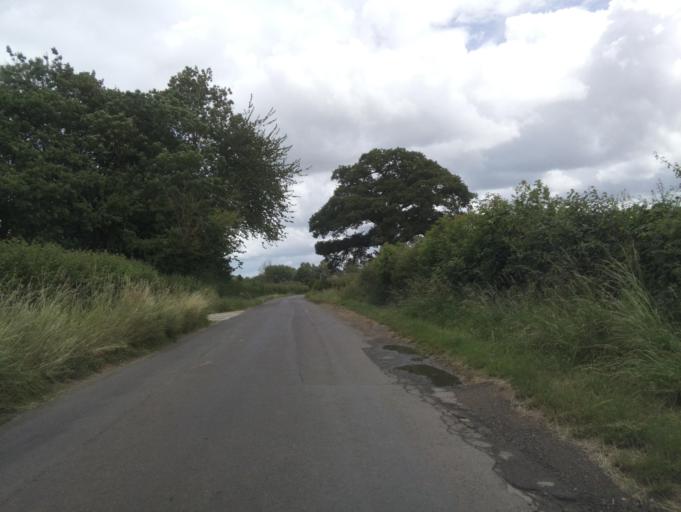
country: GB
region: England
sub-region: Wiltshire
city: Malmesbury
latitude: 51.5408
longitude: -2.0659
